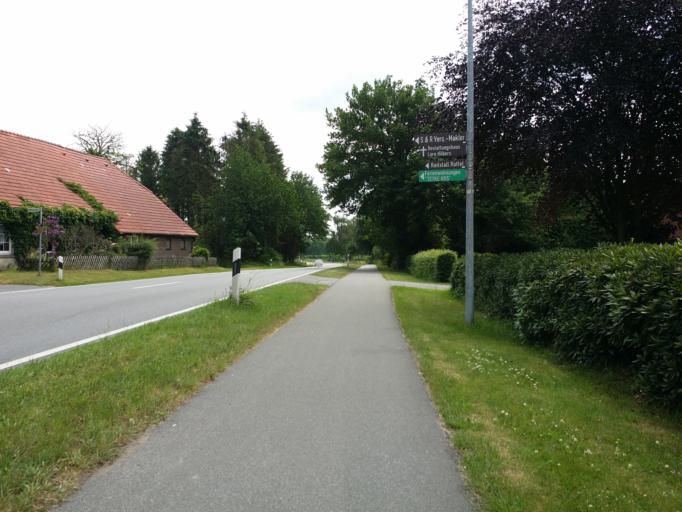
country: DE
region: Lower Saxony
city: Zetel
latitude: 53.3928
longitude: 7.9298
